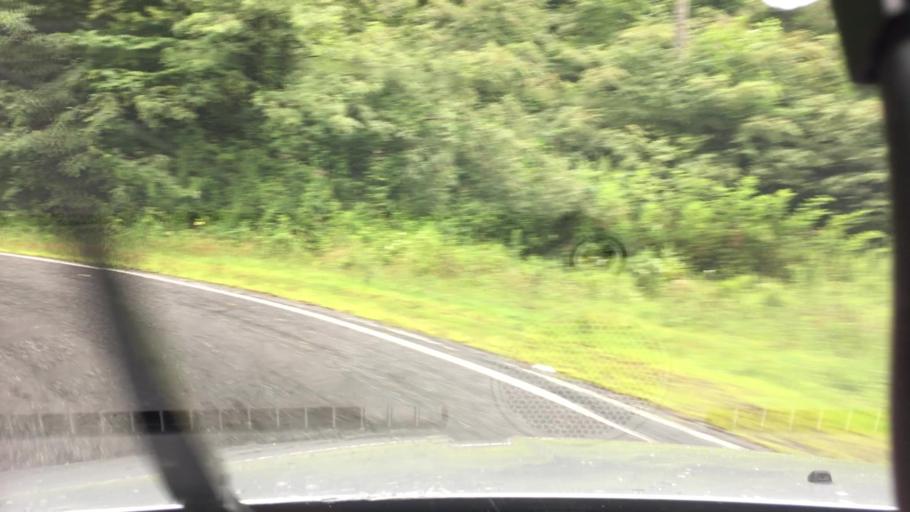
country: US
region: North Carolina
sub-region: Madison County
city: Mars Hill
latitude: 35.9146
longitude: -82.4822
